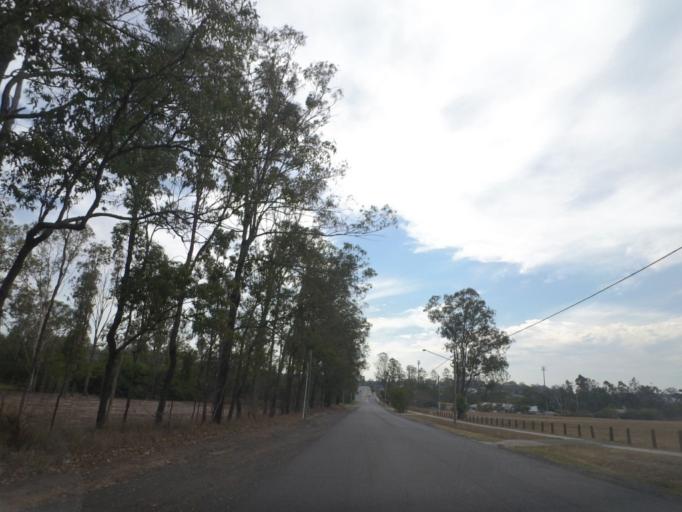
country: AU
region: Queensland
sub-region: Brisbane
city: Richlands
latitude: -27.5930
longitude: 152.9537
